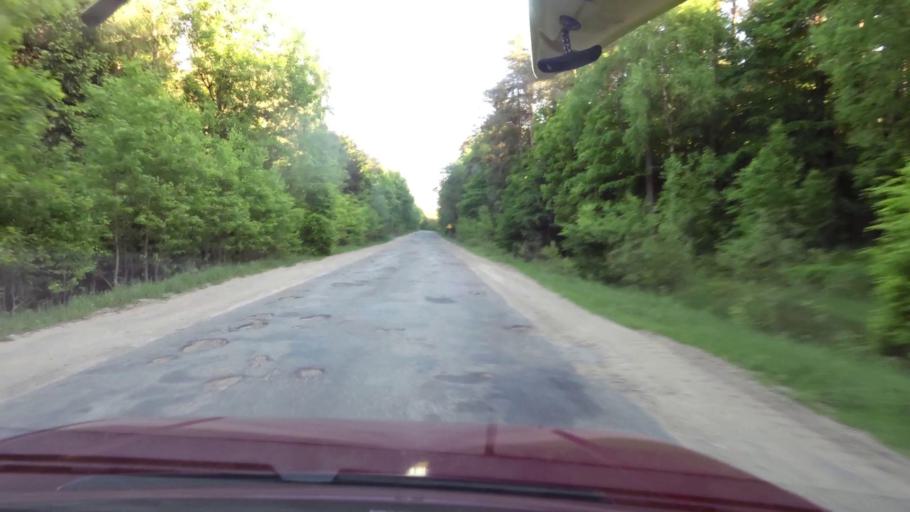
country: PL
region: West Pomeranian Voivodeship
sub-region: Powiat szczecinecki
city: Bialy Bor
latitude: 53.9278
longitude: 16.8019
